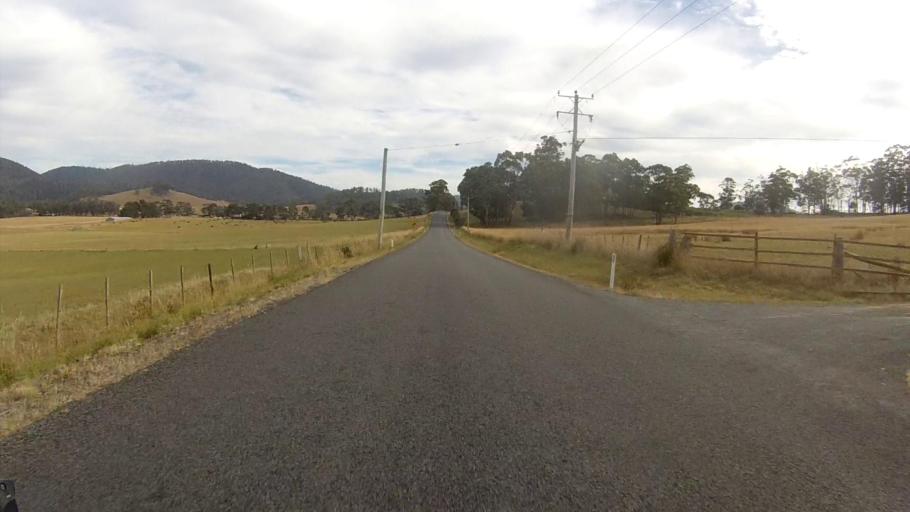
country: AU
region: Tasmania
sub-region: Sorell
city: Sorell
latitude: -42.7991
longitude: 147.7937
